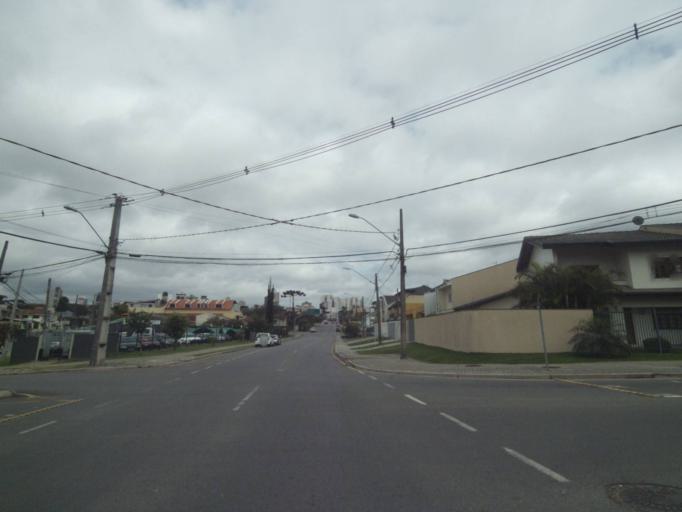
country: BR
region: Parana
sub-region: Pinhais
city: Pinhais
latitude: -25.4353
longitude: -49.2281
